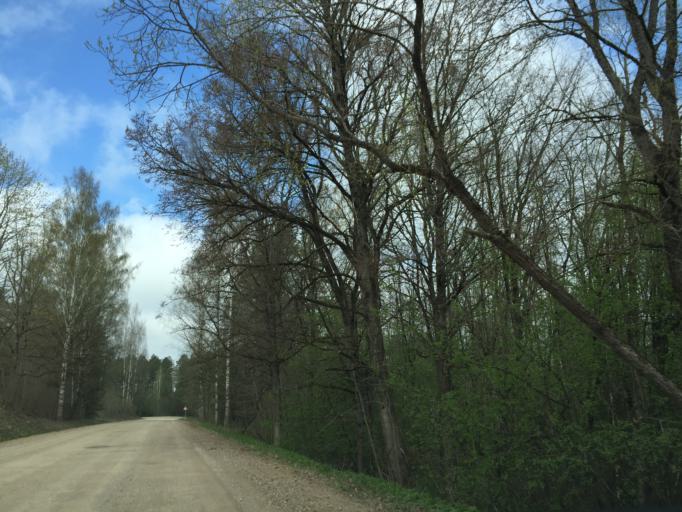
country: LV
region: Apes Novads
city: Ape
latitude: 57.5248
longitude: 26.3792
